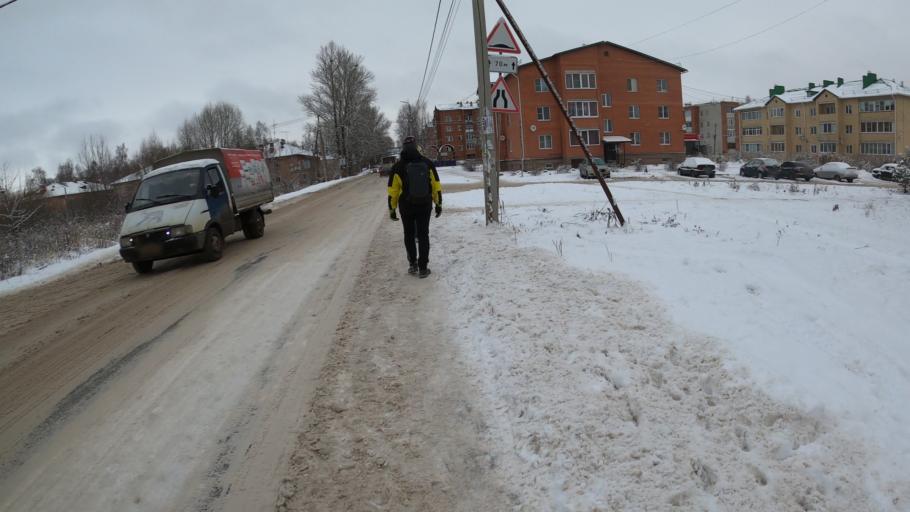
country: RU
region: Jaroslavl
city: Pereslavl'-Zalesskiy
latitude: 56.7382
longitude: 38.8865
